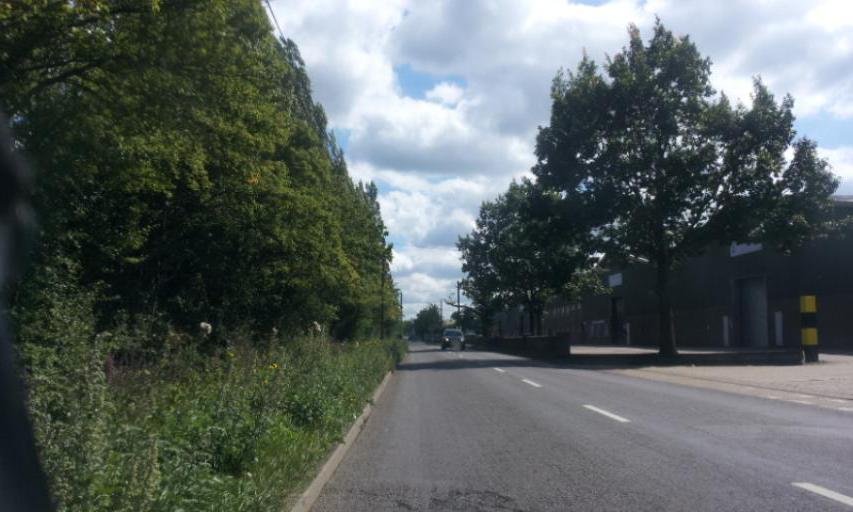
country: GB
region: England
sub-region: Kent
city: Marden
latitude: 51.1800
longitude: 0.4881
